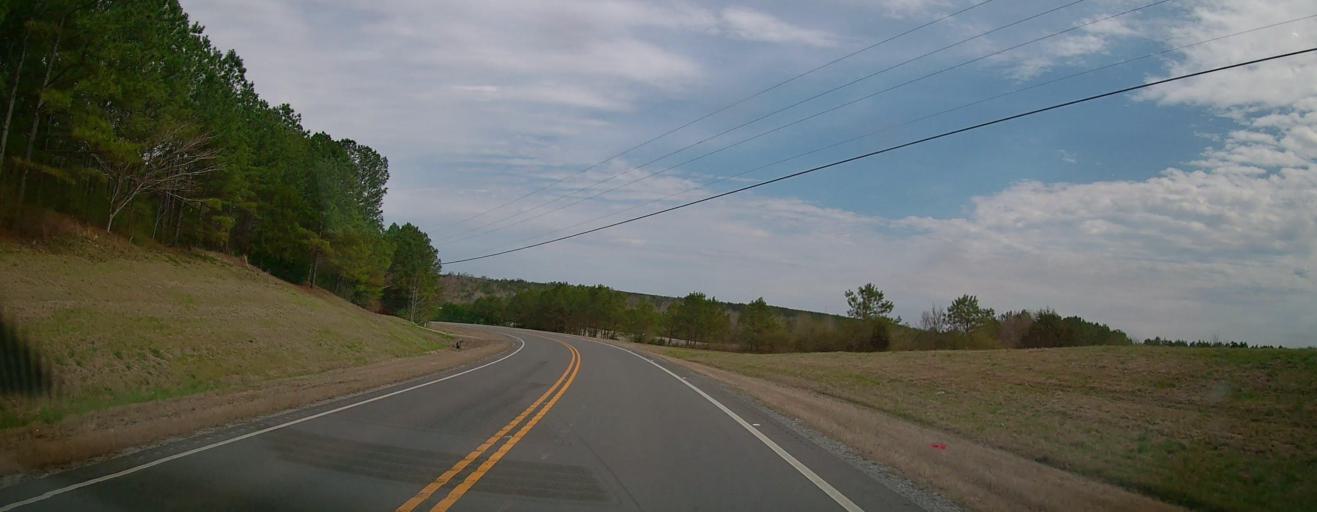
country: US
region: Alabama
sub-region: Walker County
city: Carbon Hill
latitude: 33.8650
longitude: -87.4092
